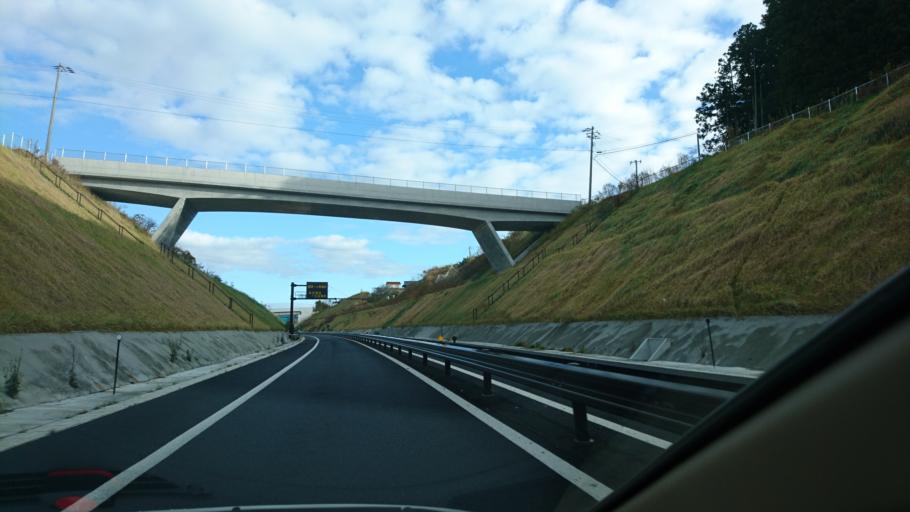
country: JP
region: Iwate
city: Ofunato
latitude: 38.8773
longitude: 141.5843
